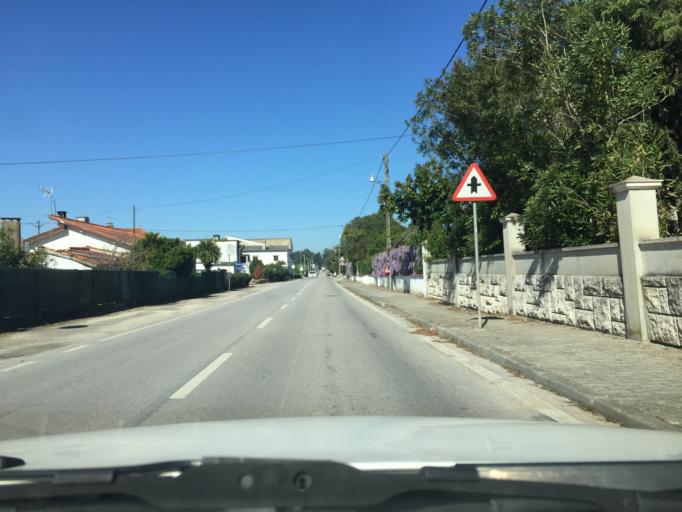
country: PT
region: Coimbra
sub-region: Cantanhede
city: Cantanhede
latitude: 40.4202
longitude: -8.5703
